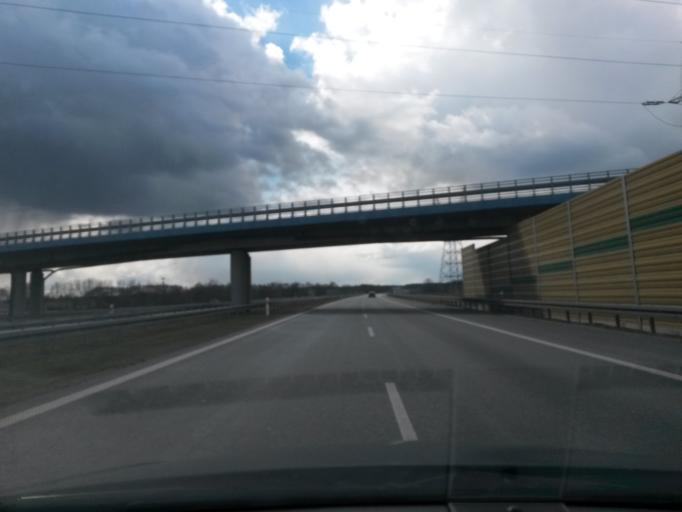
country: PL
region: Greater Poland Voivodeship
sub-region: Powiat koninski
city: Krzymow
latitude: 52.1435
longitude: 18.4066
